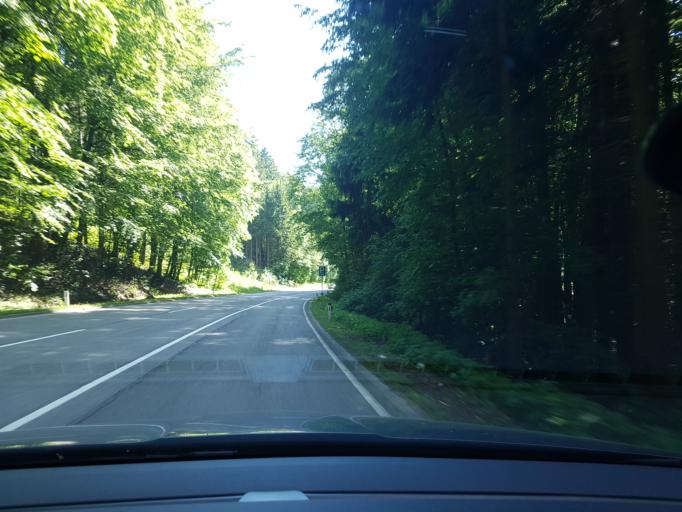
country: AT
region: Salzburg
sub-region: Politischer Bezirk Salzburg-Umgebung
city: Mattsee
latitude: 47.9673
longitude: 13.1150
